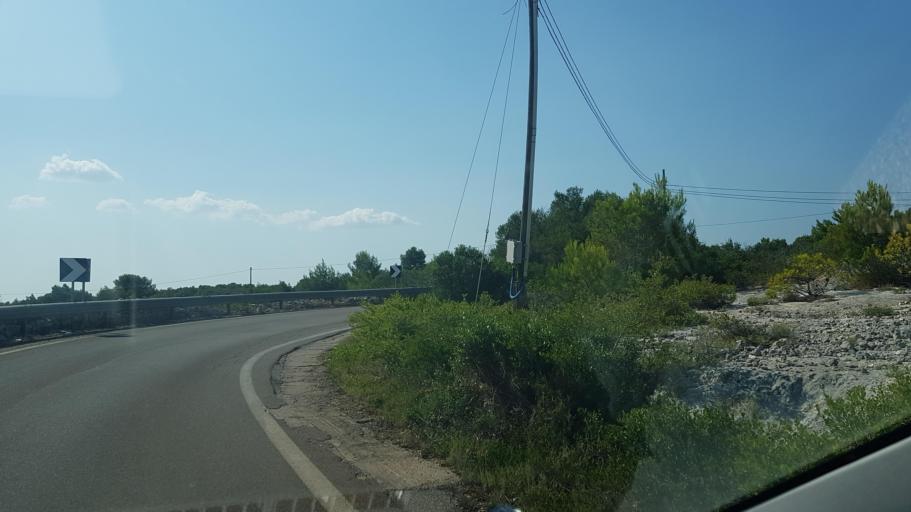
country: IT
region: Apulia
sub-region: Provincia di Lecce
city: Gemini
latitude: 39.8578
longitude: 18.2036
